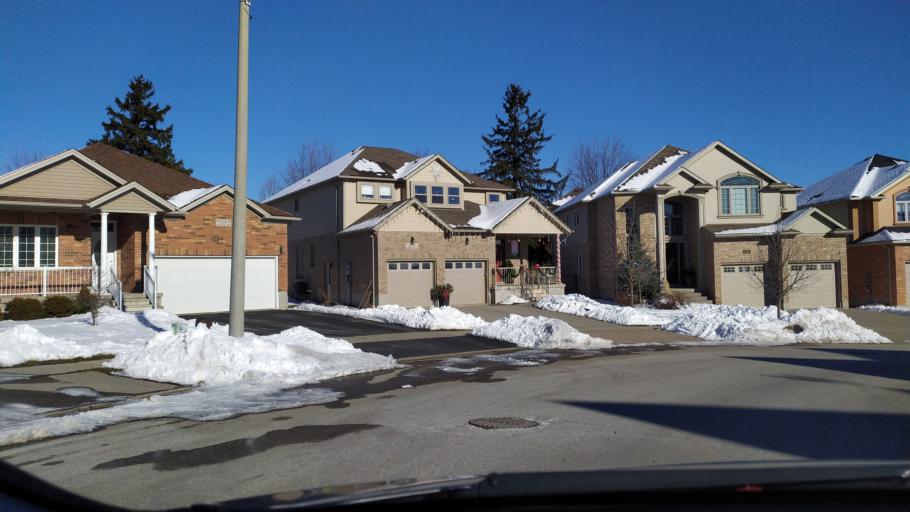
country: CA
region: Ontario
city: Waterloo
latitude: 43.4474
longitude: -80.5660
